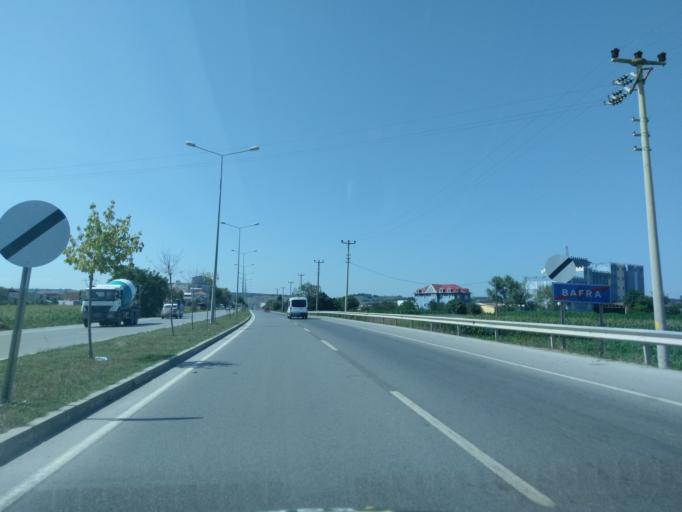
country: TR
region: Samsun
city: Bafra
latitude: 41.5722
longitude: 35.8703
